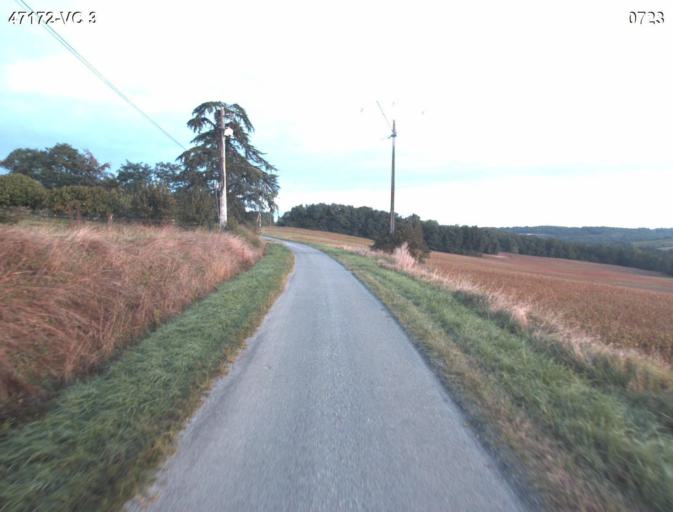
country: FR
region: Aquitaine
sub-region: Departement du Lot-et-Garonne
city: Sainte-Colombe-en-Bruilhois
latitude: 44.1638
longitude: 0.4944
